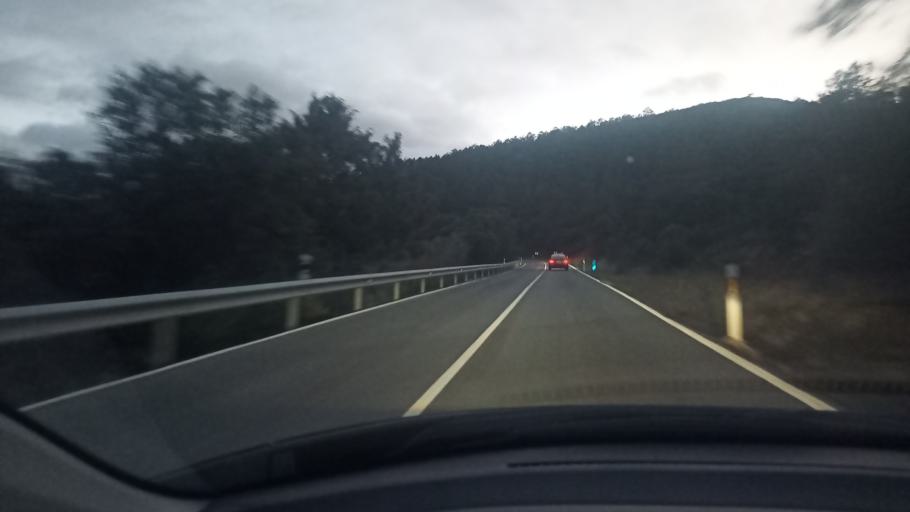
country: ES
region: Madrid
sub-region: Provincia de Madrid
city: Robledo de Chavela
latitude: 40.4586
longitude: -4.2634
